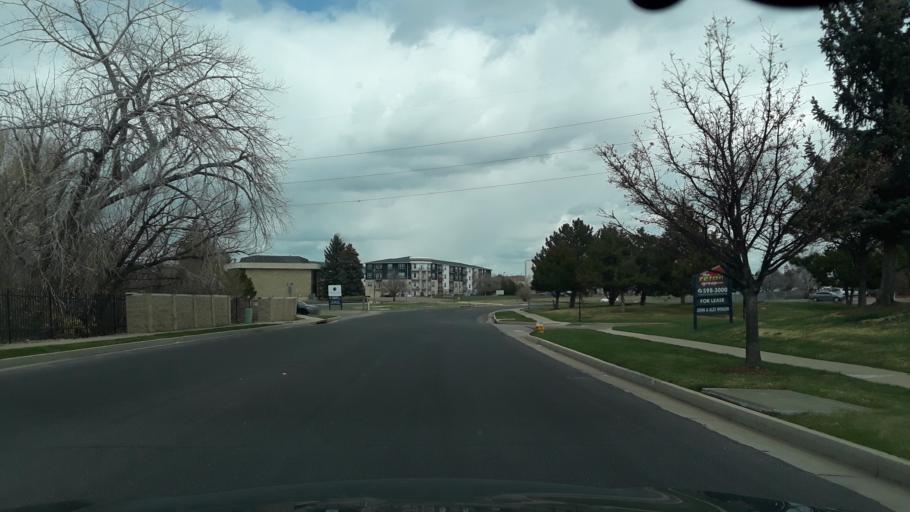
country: US
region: Colorado
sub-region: El Paso County
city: Air Force Academy
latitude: 38.9435
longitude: -104.8038
